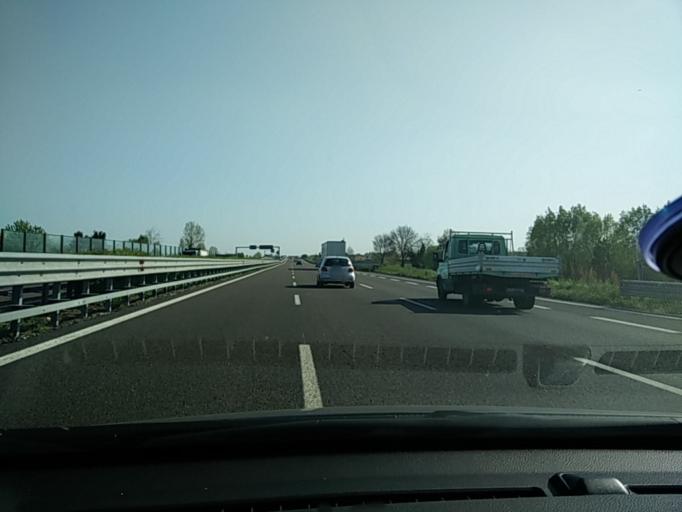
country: IT
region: Veneto
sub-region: Provincia di Venezia
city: Marcon-Gaggio-Colmello
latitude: 45.5647
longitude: 12.2743
